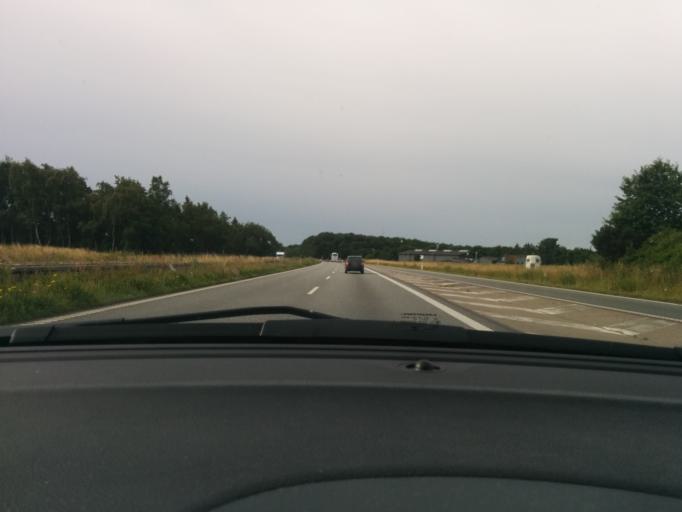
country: DK
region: Zealand
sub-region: Koge Kommune
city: Ejby
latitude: 55.4688
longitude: 12.1240
